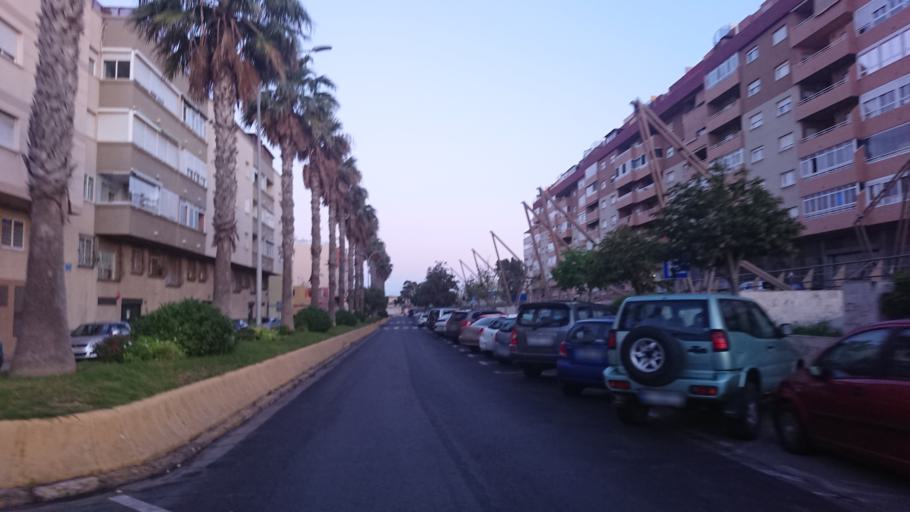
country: ES
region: Melilla
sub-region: Melilla
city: Melilla
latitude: 35.2745
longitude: -2.9472
